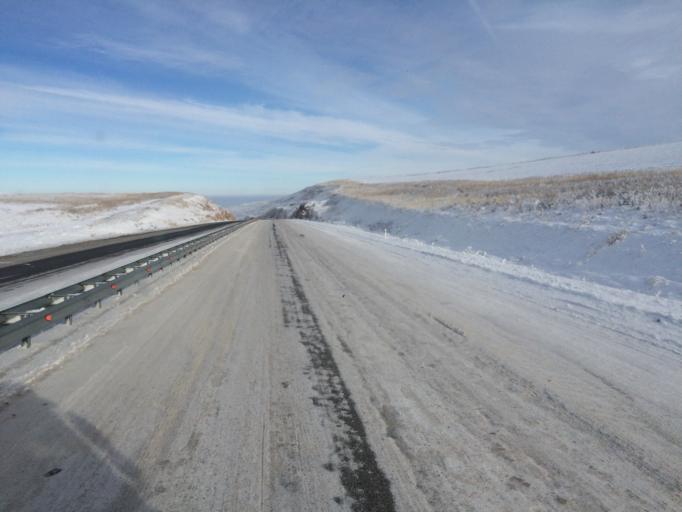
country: KZ
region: Zhambyl
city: Georgiyevka
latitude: 43.4057
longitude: 74.8597
